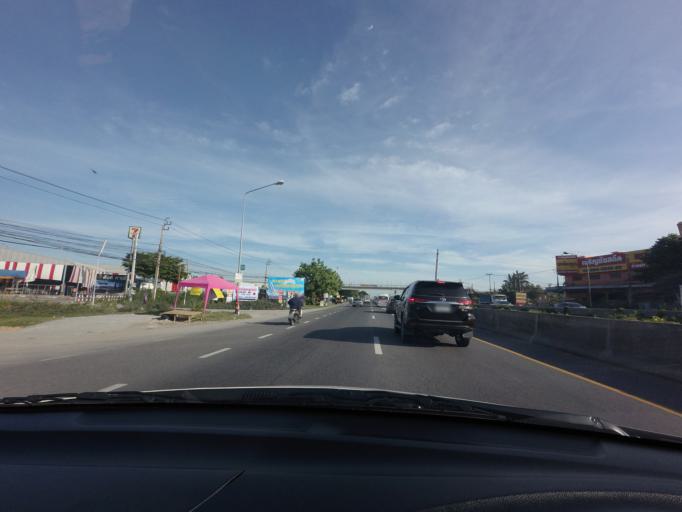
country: TH
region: Nonthaburi
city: Bang Bua Thong
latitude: 13.9516
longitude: 100.4095
